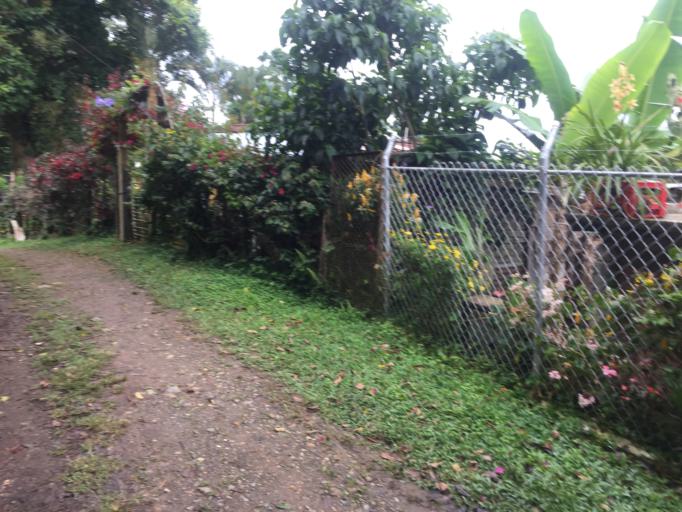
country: CO
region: Valle del Cauca
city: Cali
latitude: 3.4623
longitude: -76.6351
